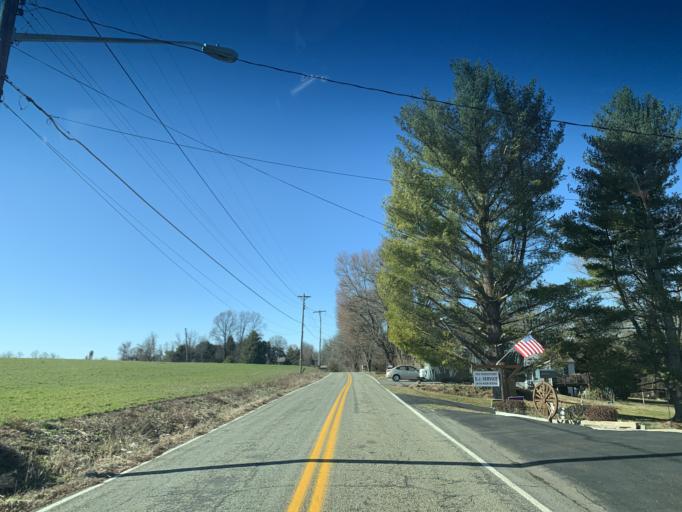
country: US
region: Maryland
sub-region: Cecil County
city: Rising Sun
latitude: 39.6835
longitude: -76.1017
